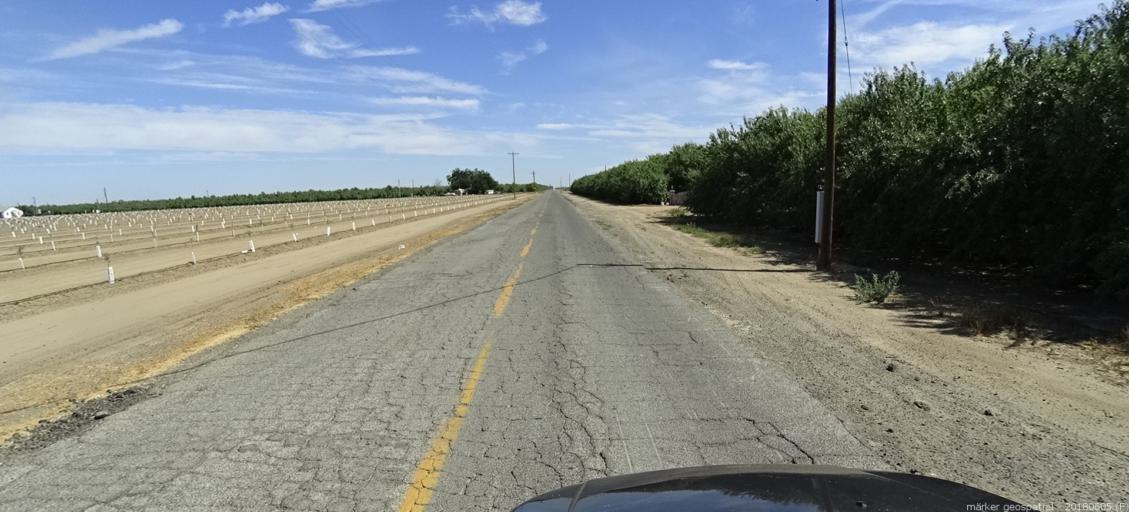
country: US
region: California
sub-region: Madera County
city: Chowchilla
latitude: 37.0228
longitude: -120.3833
